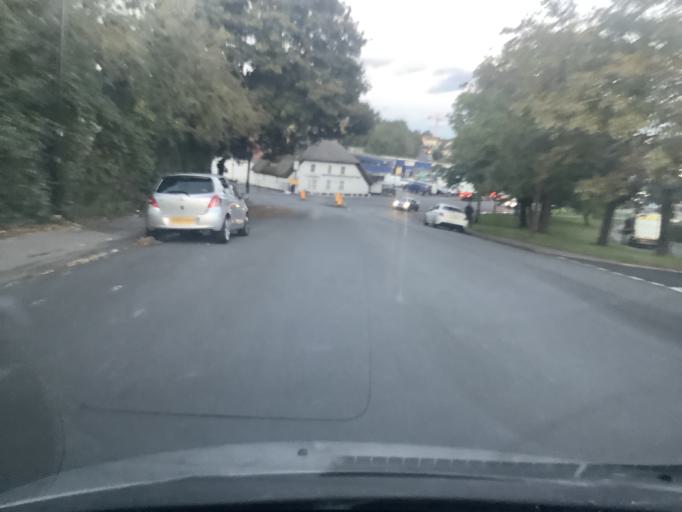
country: GB
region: England
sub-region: Hampshire
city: Marchwood
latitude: 50.9266
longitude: -1.4439
